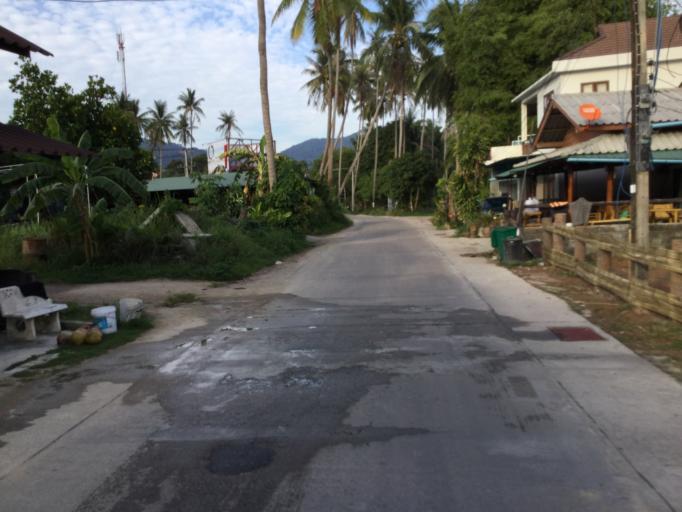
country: TH
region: Surat Thani
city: Ko Pha-Ngan
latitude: 9.6995
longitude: 100.0226
